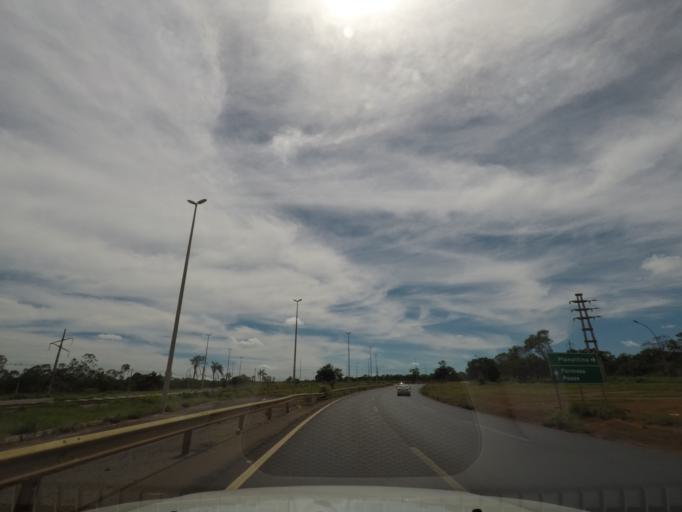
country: BR
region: Goias
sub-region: Planaltina
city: Planaltina
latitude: -15.5950
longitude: -47.6567
